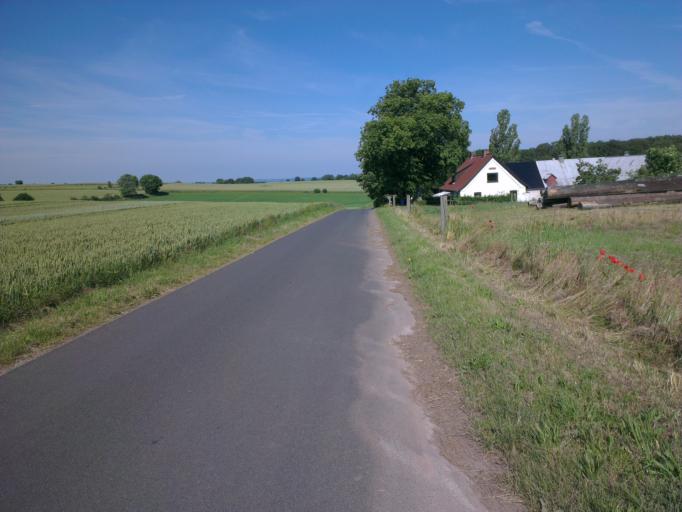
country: DK
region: Capital Region
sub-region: Frederikssund Kommune
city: Skibby
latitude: 55.7846
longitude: 11.8809
